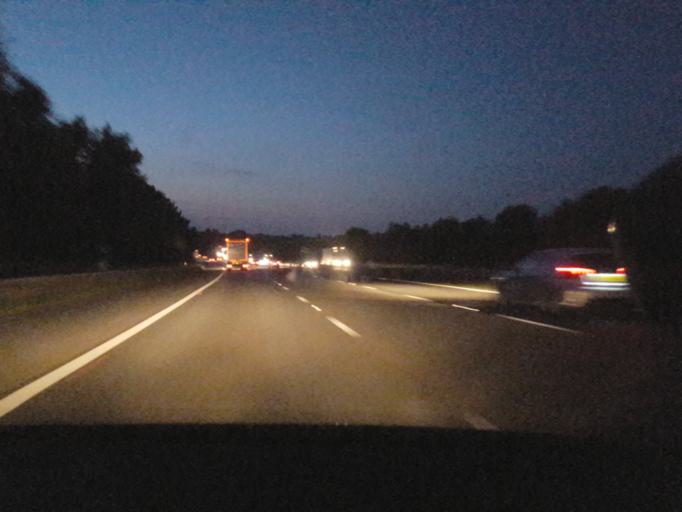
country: GB
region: England
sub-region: Leicestershire
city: Markfield
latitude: 52.7262
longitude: -1.2823
